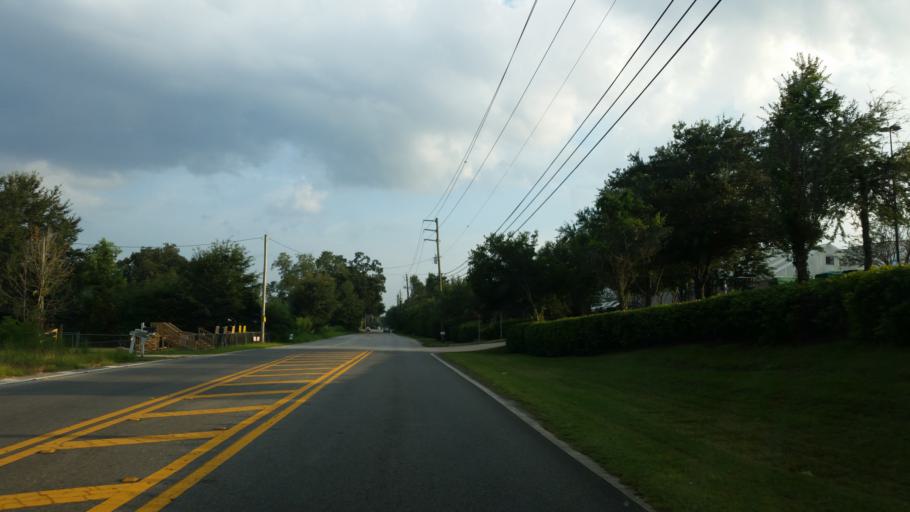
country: US
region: Florida
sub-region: Santa Rosa County
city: Pace
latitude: 30.6020
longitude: -87.1154
